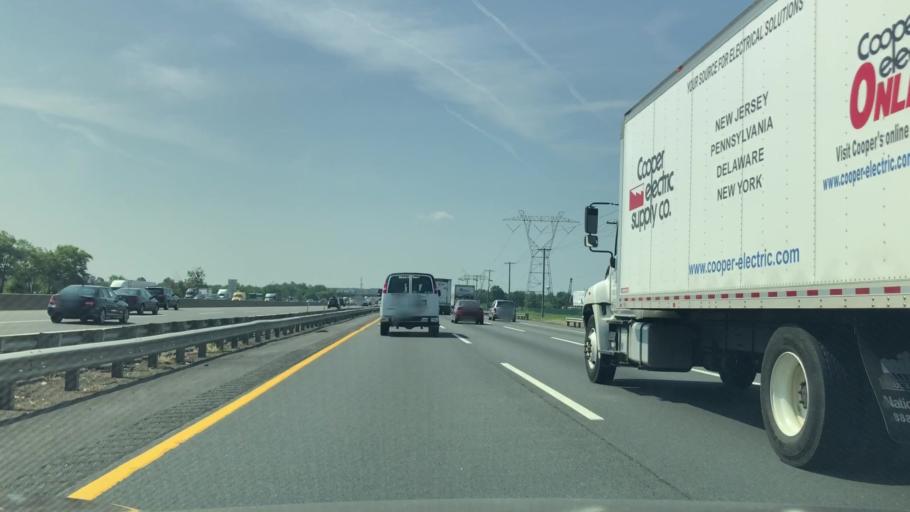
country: US
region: New Jersey
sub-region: Middlesex County
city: Jamesburg
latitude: 40.3812
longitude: -74.4615
